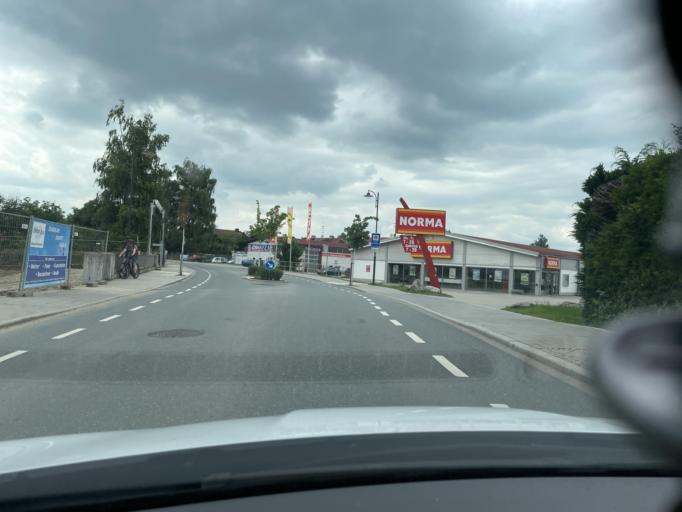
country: DE
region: Bavaria
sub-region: Upper Bavaria
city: Haag in Oberbayern
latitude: 48.1632
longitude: 12.1740
